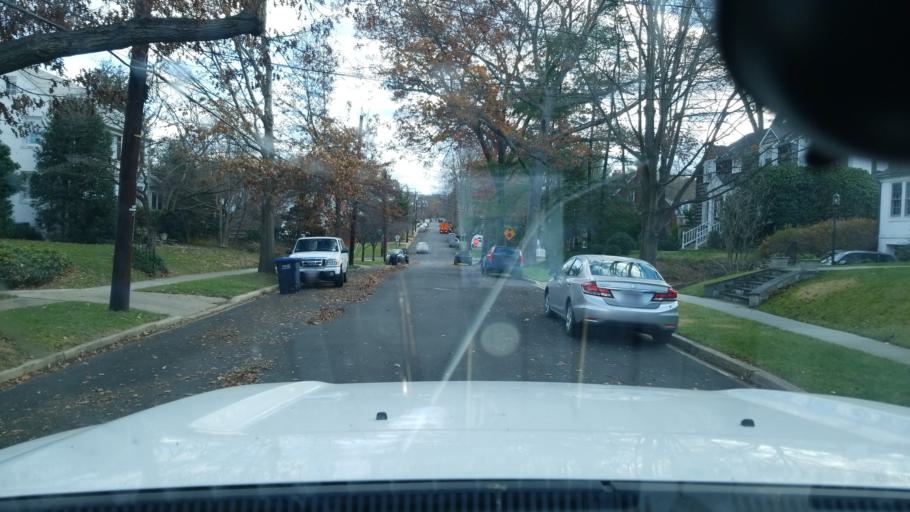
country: US
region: Maryland
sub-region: Montgomery County
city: Friendship Village
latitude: 38.9413
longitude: -77.0956
